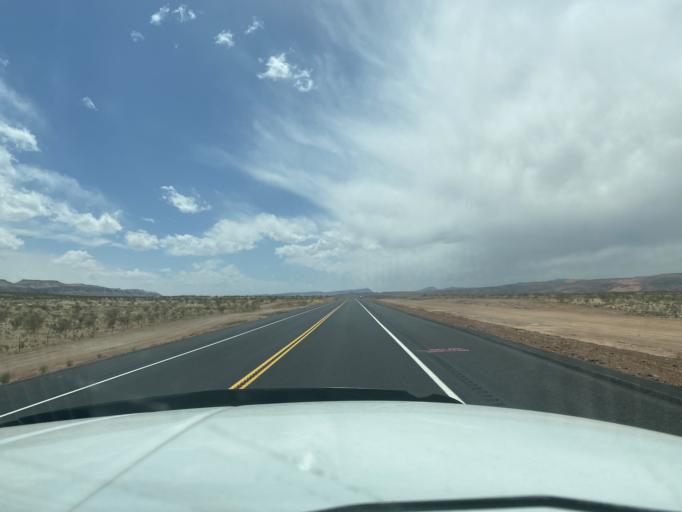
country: US
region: Utah
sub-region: Washington County
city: Hurricane
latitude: 37.1532
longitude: -113.3458
